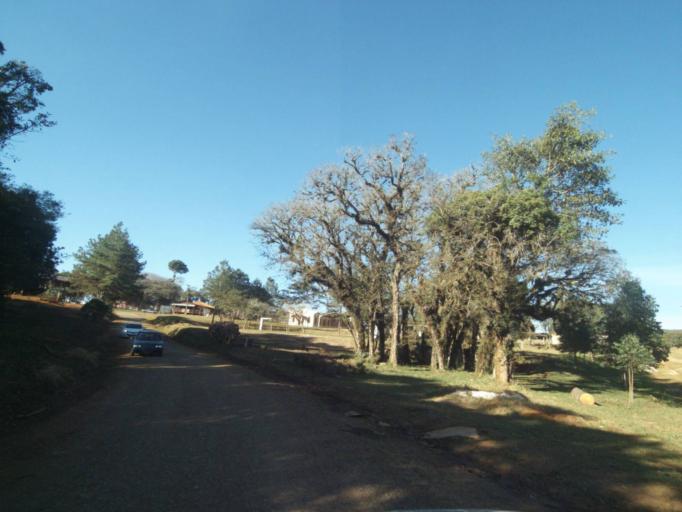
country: BR
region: Parana
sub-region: Tibagi
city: Tibagi
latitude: -24.5413
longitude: -50.4993
